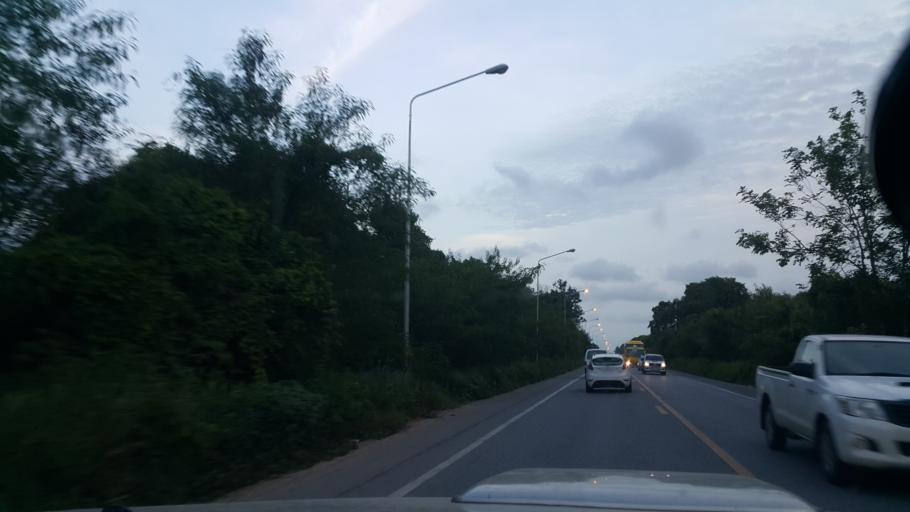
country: TH
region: Rayong
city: Ban Chang
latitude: 12.7183
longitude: 100.9939
